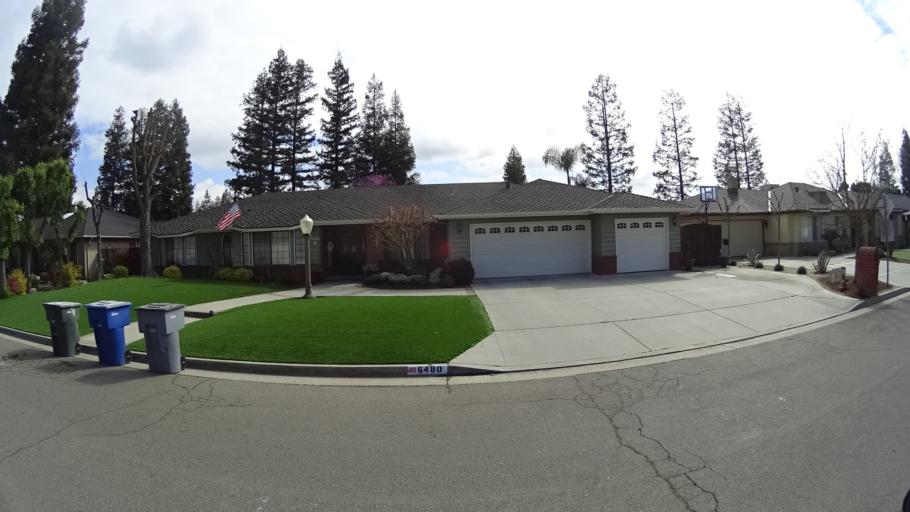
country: US
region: California
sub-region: Fresno County
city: Fresno
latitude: 36.8314
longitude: -119.8574
